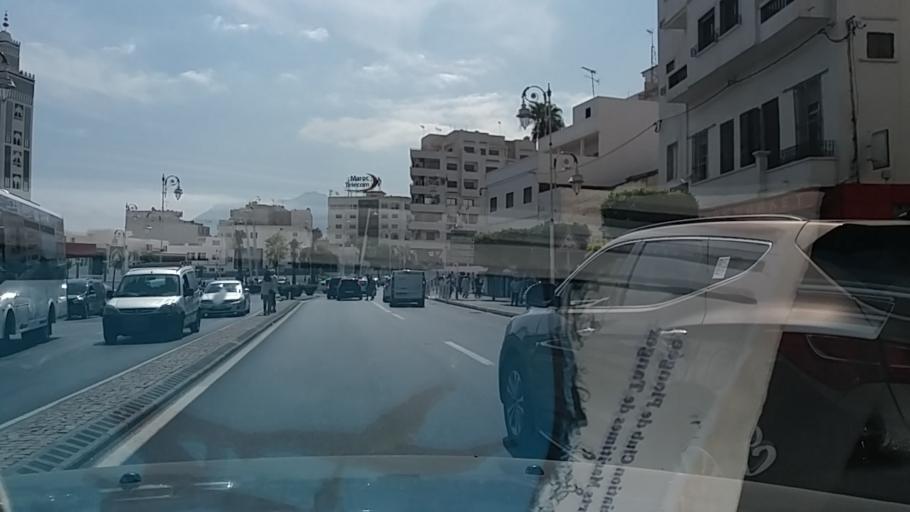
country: MA
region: Tanger-Tetouan
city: Tetouan
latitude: 35.5723
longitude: -5.3598
